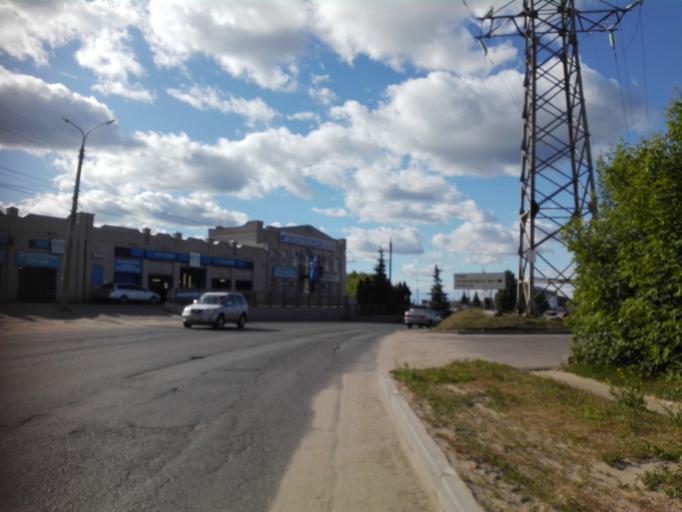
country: RU
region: Orjol
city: Orel
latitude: 52.9386
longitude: 36.0330
